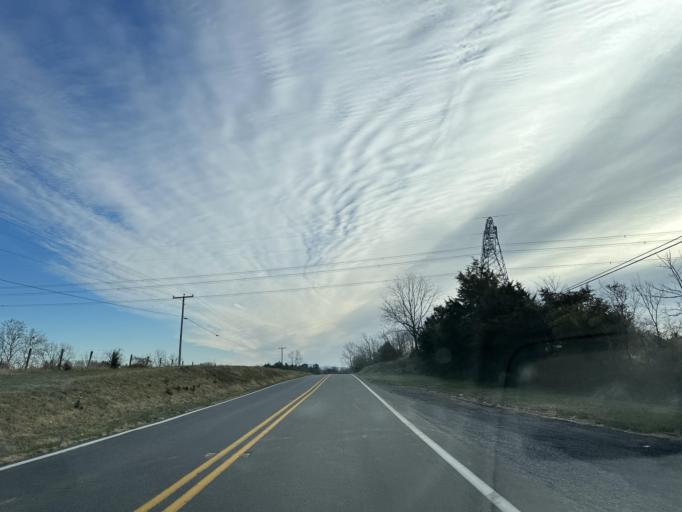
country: US
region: Virginia
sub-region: Rockingham County
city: Bridgewater
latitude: 38.3706
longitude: -79.0016
